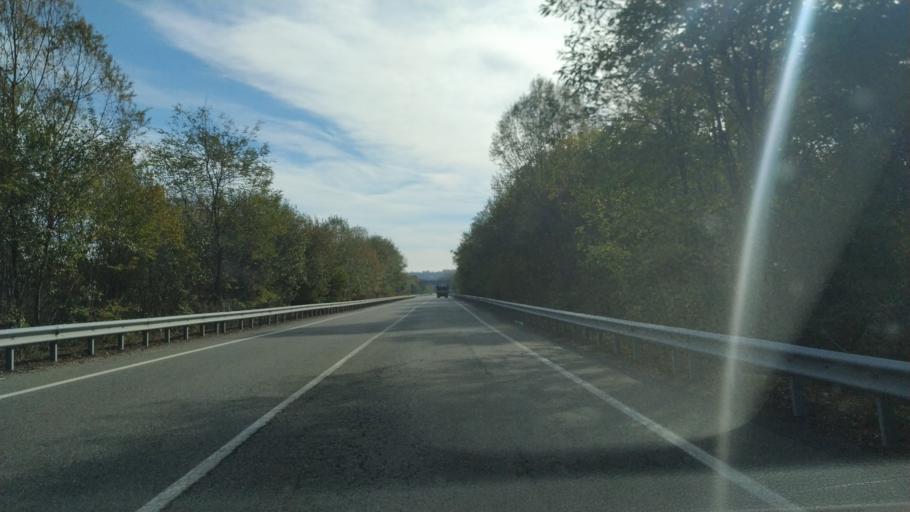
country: IT
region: Piedmont
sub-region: Provincia di Novara
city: Prato Sesia
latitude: 45.6669
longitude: 8.3623
